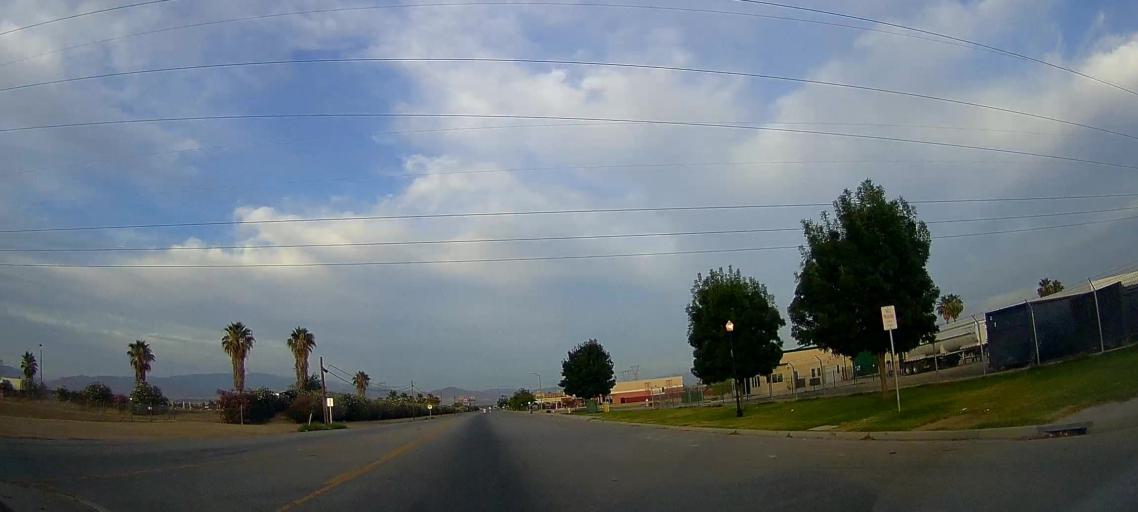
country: US
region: California
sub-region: Kern County
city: Lamont
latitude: 35.3543
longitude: -118.9229
